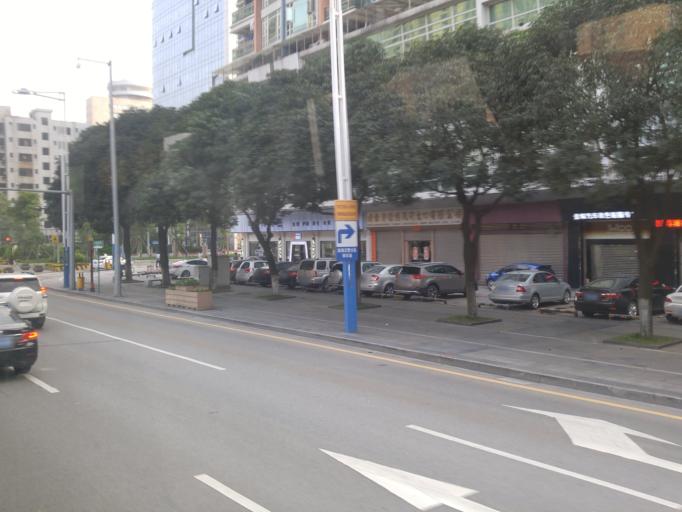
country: CN
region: Guangdong
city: Foshan
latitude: 23.0615
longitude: 113.1401
